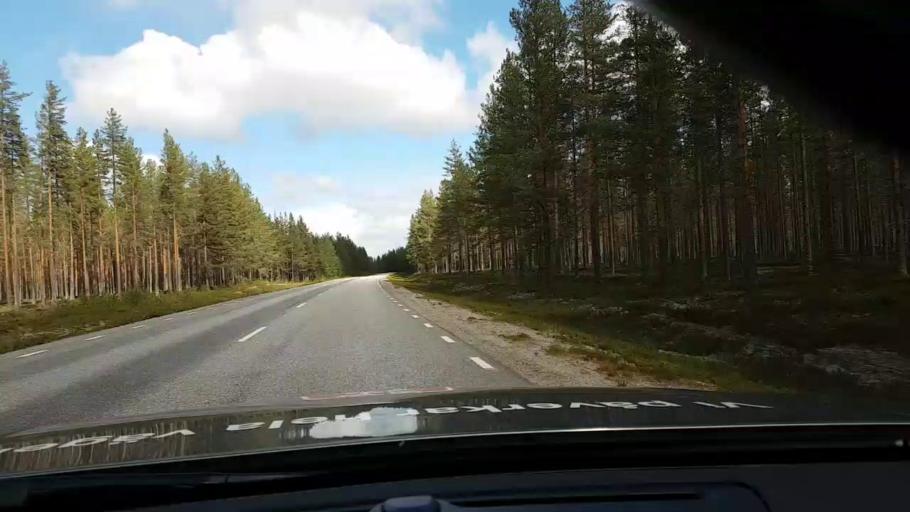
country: SE
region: Vaesternorrland
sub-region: OErnskoeldsviks Kommun
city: Bredbyn
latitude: 63.6115
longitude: 17.9015
